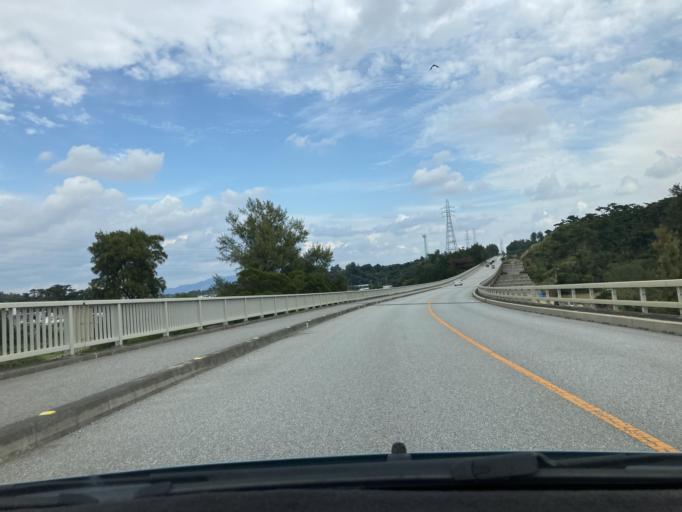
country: JP
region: Okinawa
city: Ishikawa
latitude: 26.4919
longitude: 127.8541
